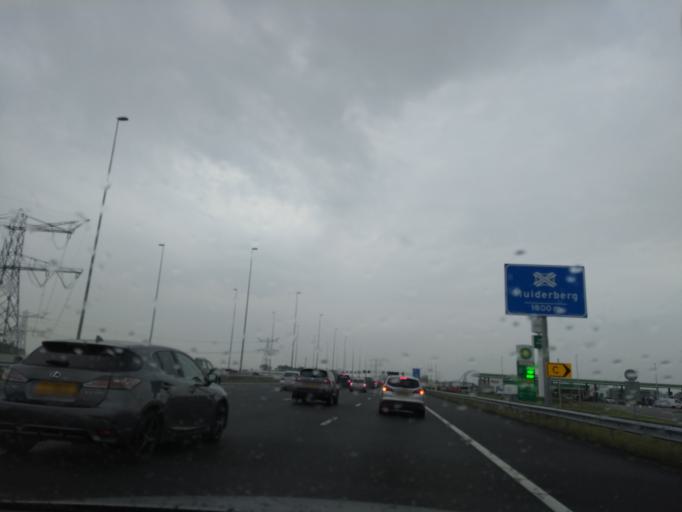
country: NL
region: North Holland
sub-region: Gemeente Weesp
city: Weesp
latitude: 52.3215
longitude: 5.0754
